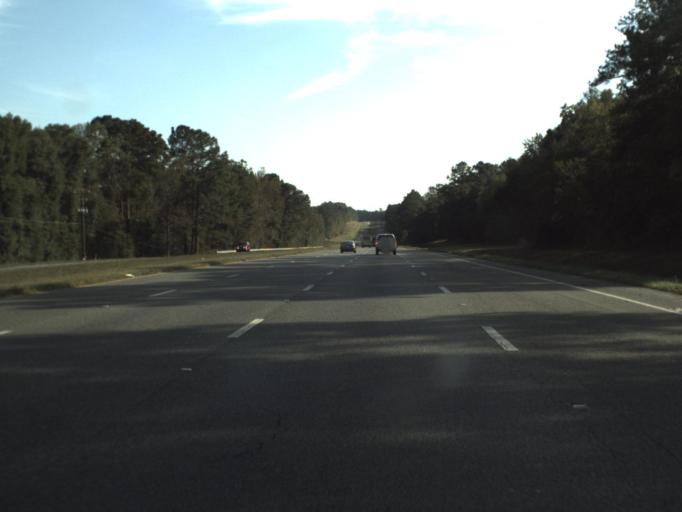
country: US
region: Florida
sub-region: Gadsden County
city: Midway
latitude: 30.5350
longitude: -84.4755
